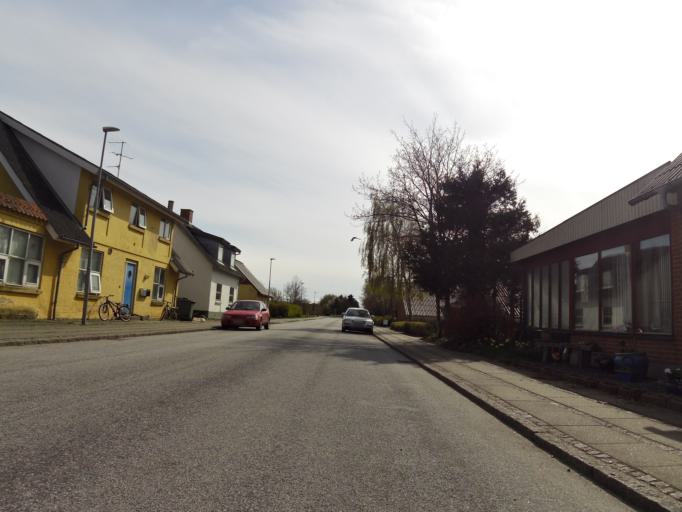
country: DK
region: Central Jutland
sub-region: Skive Kommune
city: Skive
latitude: 56.5335
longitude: 8.9320
